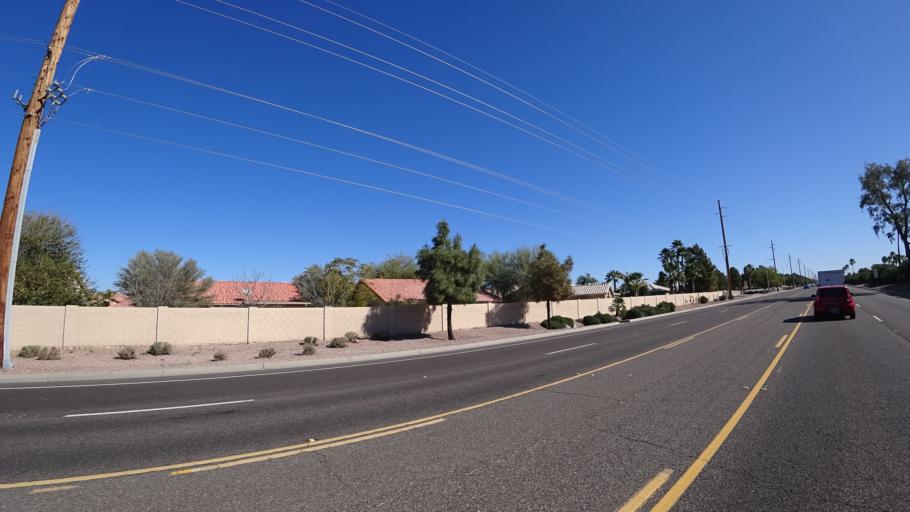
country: US
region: Arizona
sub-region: Maricopa County
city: Sun Lakes
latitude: 33.2184
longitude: -111.8510
